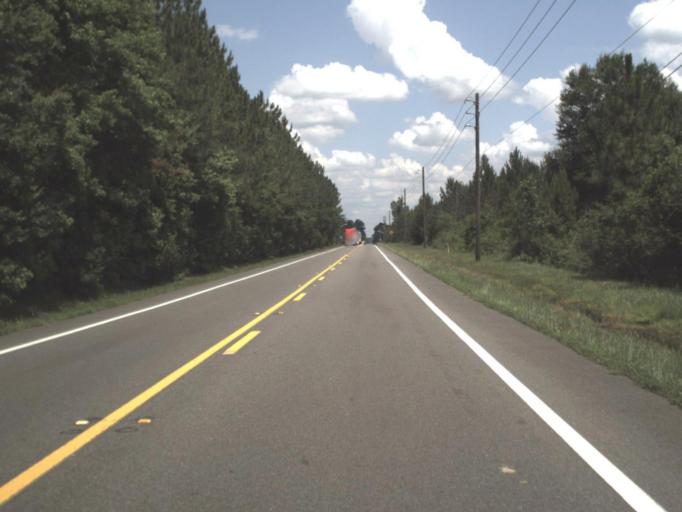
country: US
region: Florida
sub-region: Nassau County
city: Nassau Village-Ratliff
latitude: 30.4904
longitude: -81.7357
